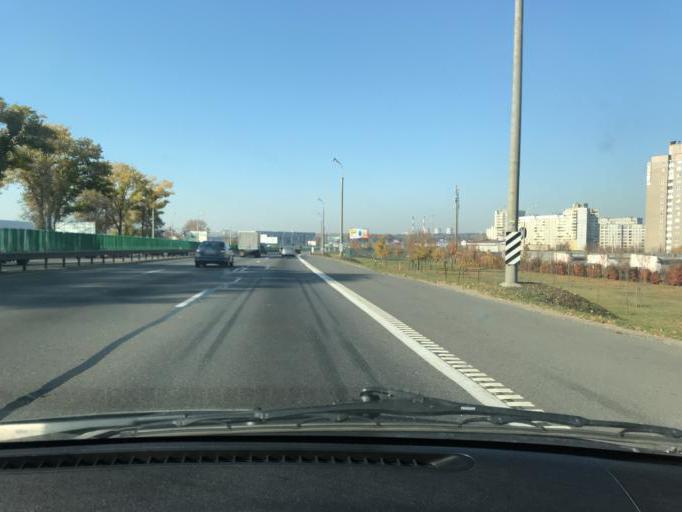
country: BY
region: Minsk
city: Malinovka
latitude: 53.8462
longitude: 27.4448
